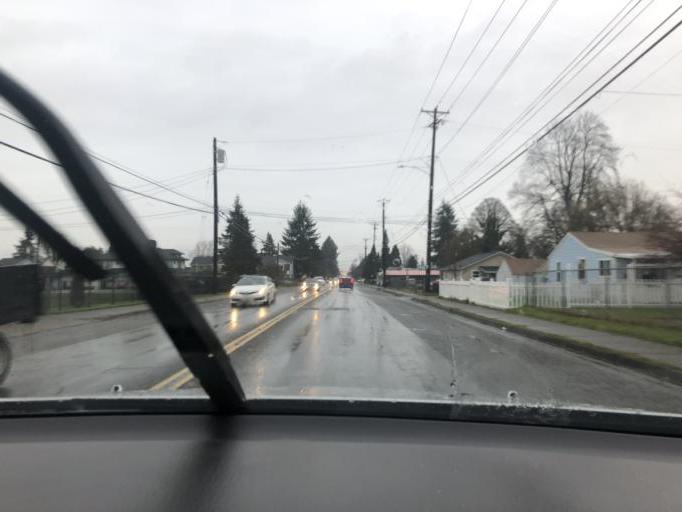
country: US
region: Washington
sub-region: Pierce County
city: Midland
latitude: 47.2037
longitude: -122.4209
